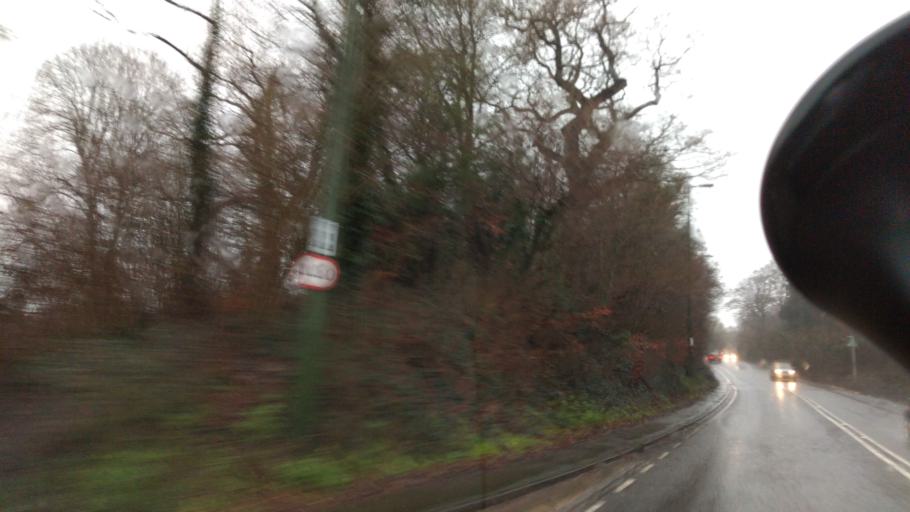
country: GB
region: England
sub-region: West Sussex
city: Arundel
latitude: 50.8528
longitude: -0.5625
